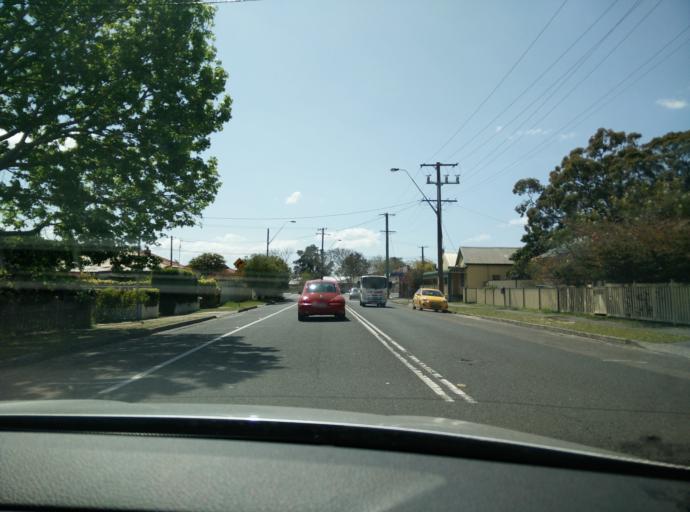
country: AU
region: New South Wales
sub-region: Gosford Shire
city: Blackwall
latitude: -33.4930
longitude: 151.3120
